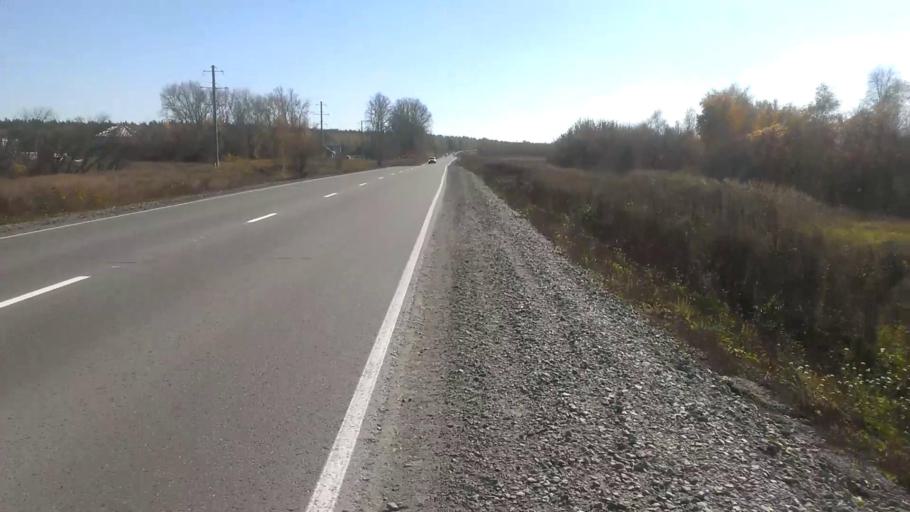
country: RU
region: Altai Krai
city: Sannikovo
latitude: 53.3100
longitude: 83.9666
